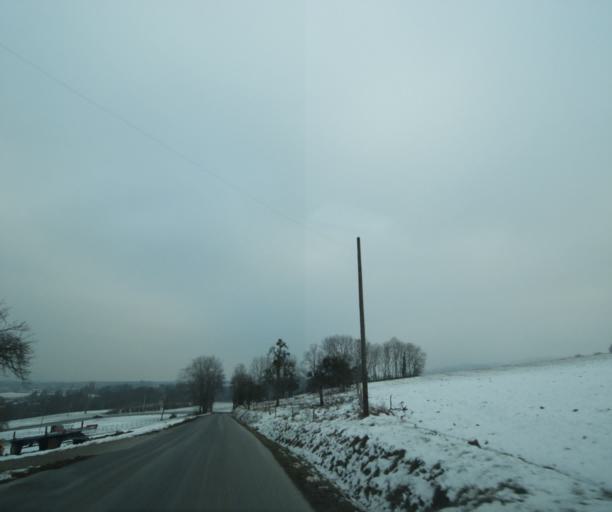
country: FR
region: Rhone-Alpes
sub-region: Departement de la Haute-Savoie
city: Reignier-Esery
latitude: 46.1339
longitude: 6.2542
